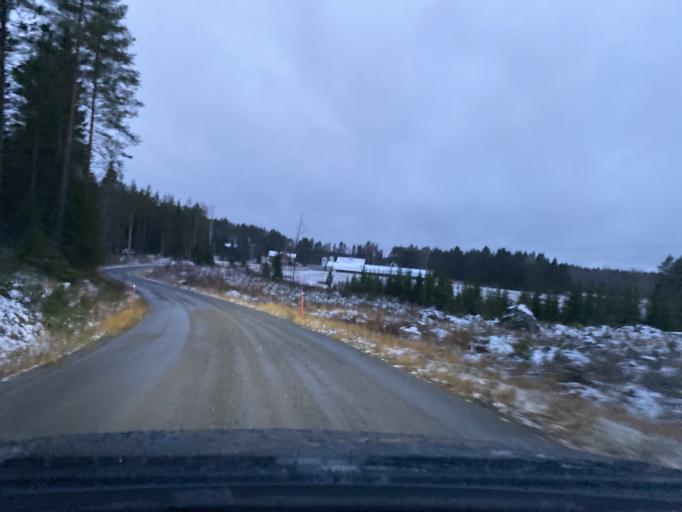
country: FI
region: Pirkanmaa
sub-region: Lounais-Pirkanmaa
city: Punkalaidun
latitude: 61.1462
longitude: 22.9660
